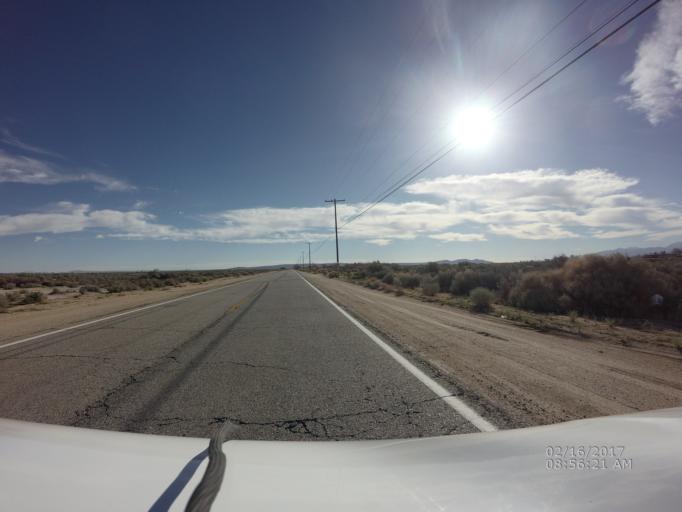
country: US
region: California
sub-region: Kern County
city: Edwards Air Force Base
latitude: 34.7637
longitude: -117.9562
